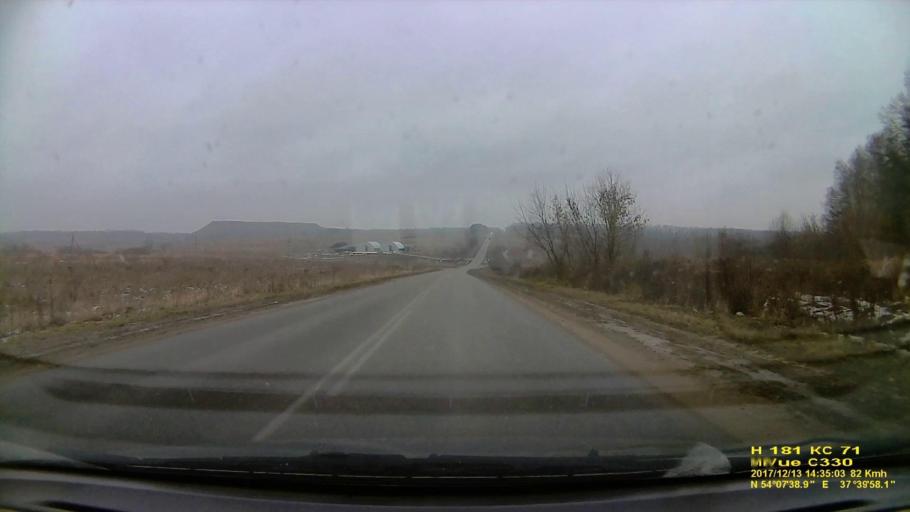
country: RU
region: Tula
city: Skuratovskiy
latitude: 54.1278
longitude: 37.6661
